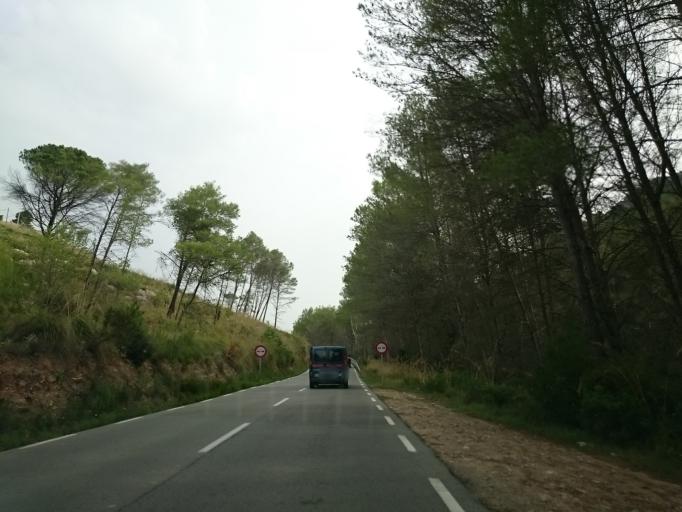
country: ES
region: Catalonia
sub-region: Provincia de Barcelona
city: Olivella
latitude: 41.3028
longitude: 1.7837
